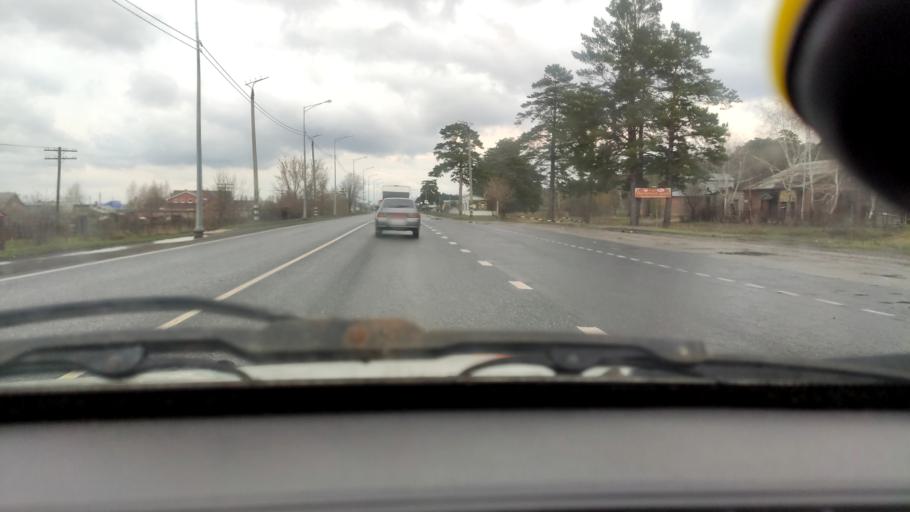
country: RU
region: Samara
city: Povolzhskiy
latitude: 53.5844
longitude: 49.5701
